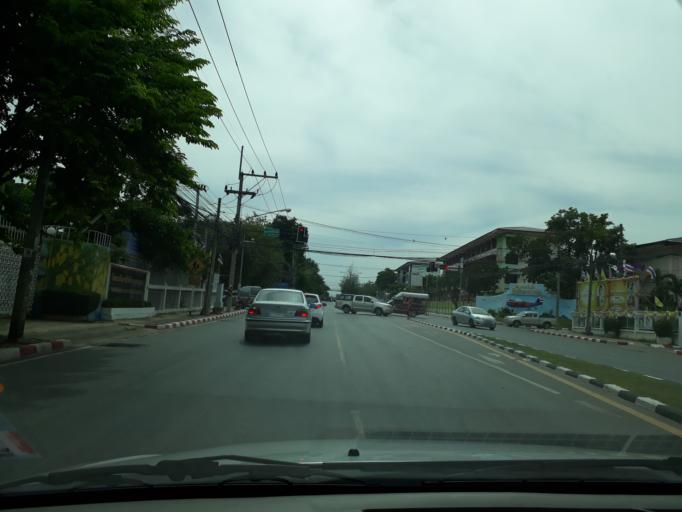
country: TH
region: Khon Kaen
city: Khon Kaen
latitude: 16.4381
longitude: 102.8392
